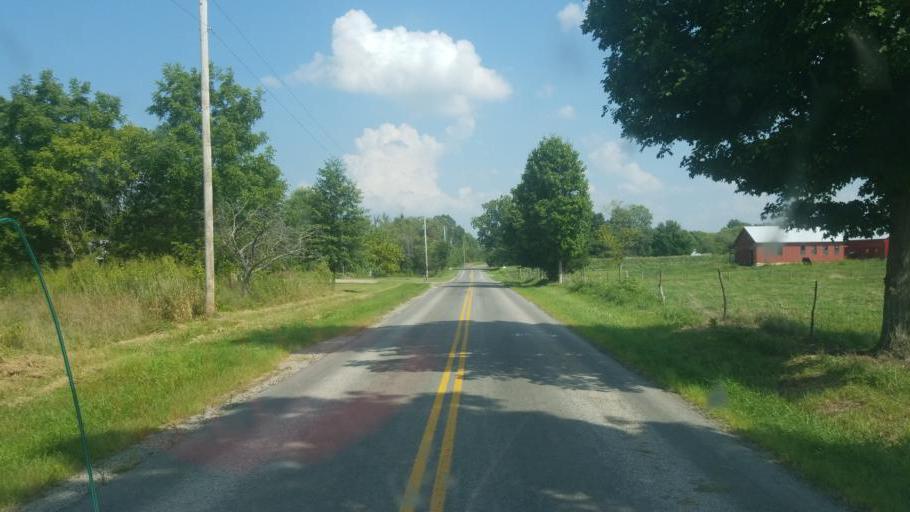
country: US
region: Ohio
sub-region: Wayne County
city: West Salem
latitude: 41.0453
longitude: -82.1575
